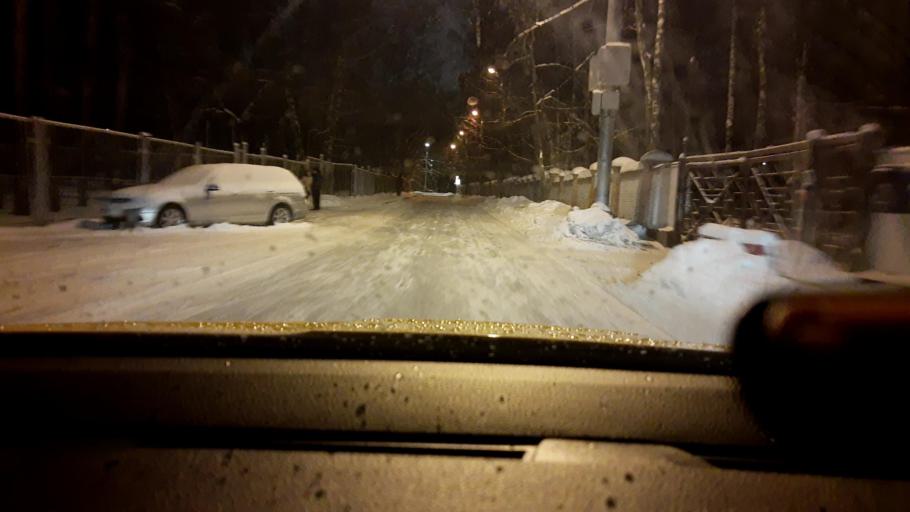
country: RU
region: Moscow
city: Rostokino
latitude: 55.8319
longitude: 37.6835
